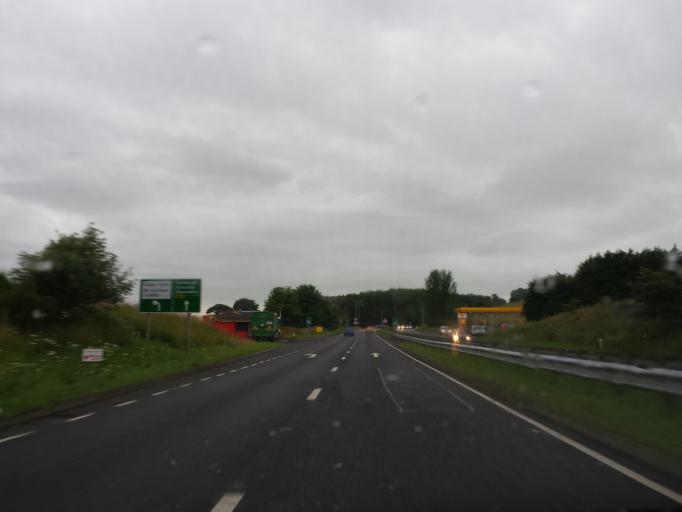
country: GB
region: Scotland
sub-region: Fife
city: Newport-On-Tay
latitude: 56.4318
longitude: -2.9332
